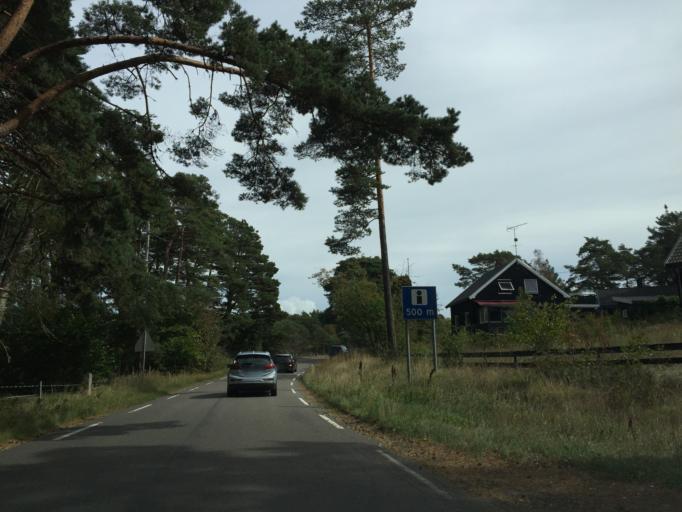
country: NO
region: Ostfold
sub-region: Hvaler
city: Skjaerhalden
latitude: 59.0342
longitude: 11.0208
